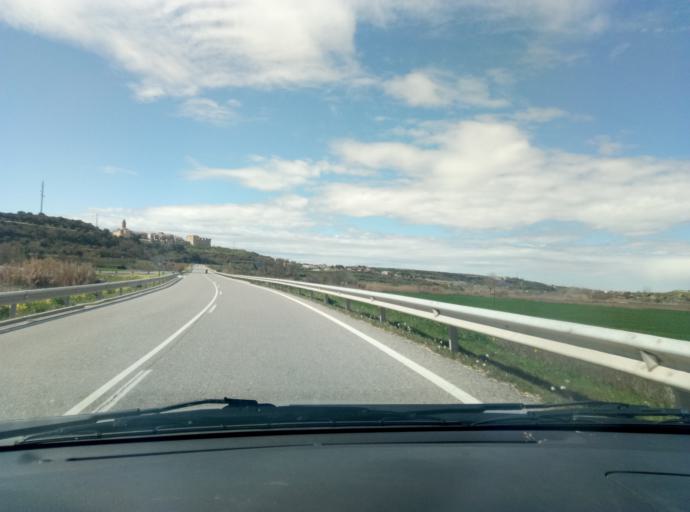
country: ES
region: Catalonia
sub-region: Provincia de Lleida
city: Vallbona de les Monges
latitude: 41.5576
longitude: 1.0467
